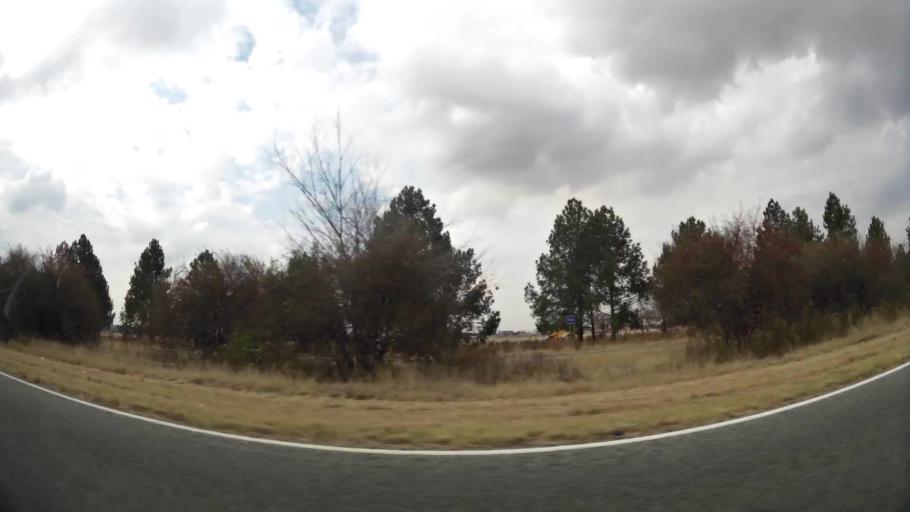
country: ZA
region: Orange Free State
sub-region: Fezile Dabi District Municipality
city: Sasolburg
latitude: -26.8068
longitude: 27.8364
